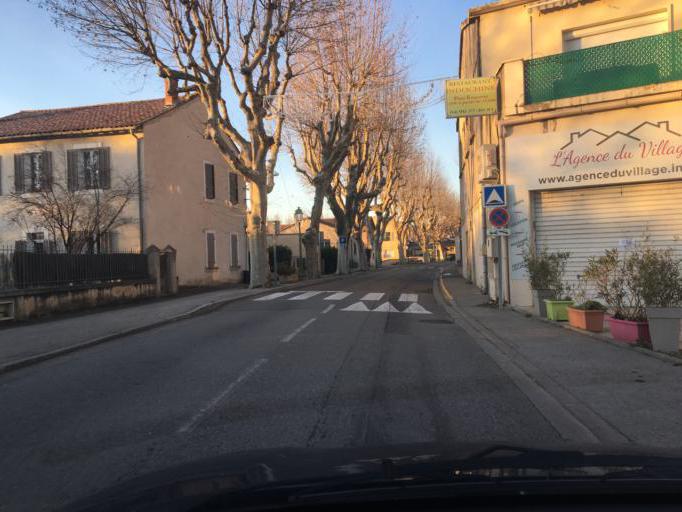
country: FR
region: Provence-Alpes-Cote d'Azur
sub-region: Departement des Bouches-du-Rhone
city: Mallemort
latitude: 43.7282
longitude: 5.1780
